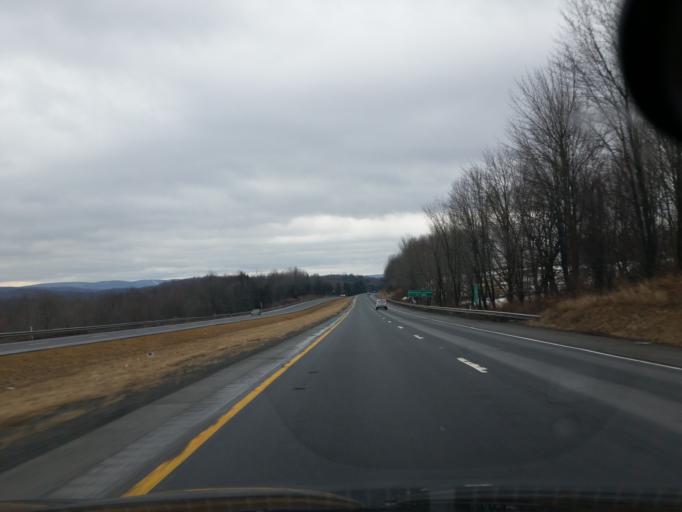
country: US
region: Pennsylvania
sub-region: Lackawanna County
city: Dalton
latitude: 41.6190
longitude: -75.6442
